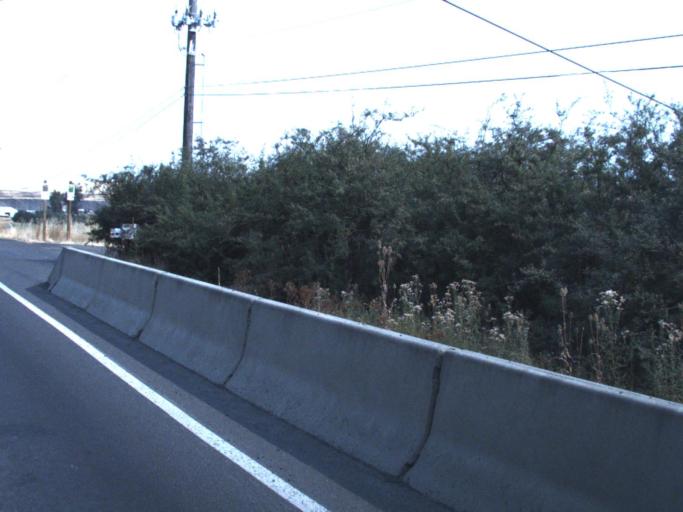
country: US
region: Washington
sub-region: Whitman County
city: Pullman
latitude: 46.7515
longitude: -117.1710
